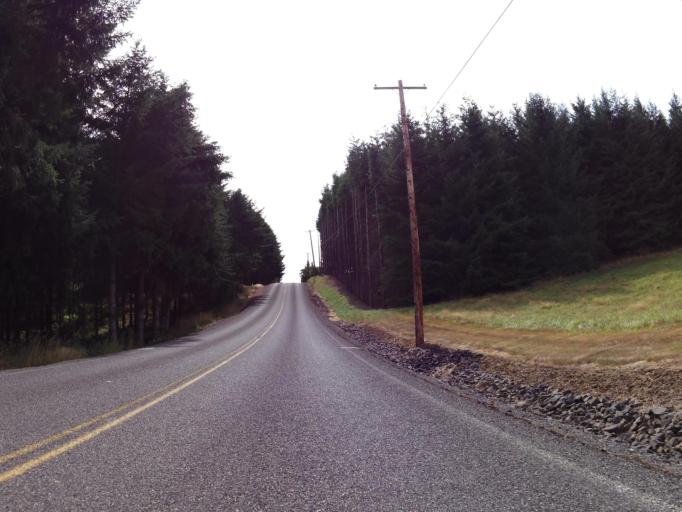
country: US
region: Washington
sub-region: Lewis County
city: Winlock
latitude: 46.5208
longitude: -122.9495
